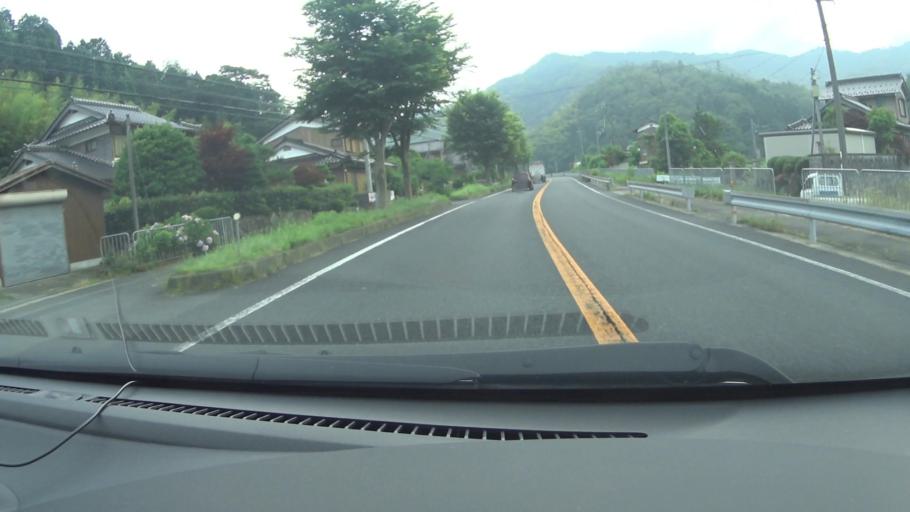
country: JP
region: Kyoto
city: Maizuru
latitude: 35.4018
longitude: 135.3225
